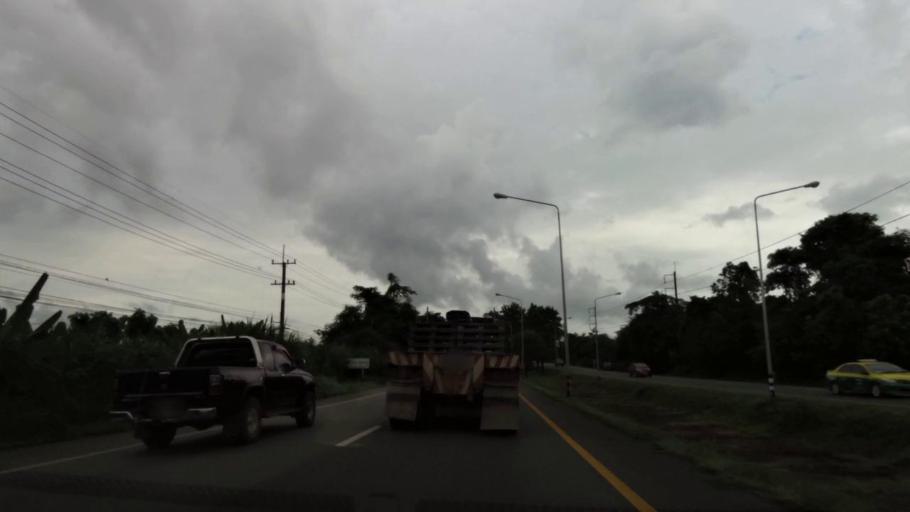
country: TH
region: Chanthaburi
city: Tha Mai
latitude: 12.6968
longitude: 101.9892
